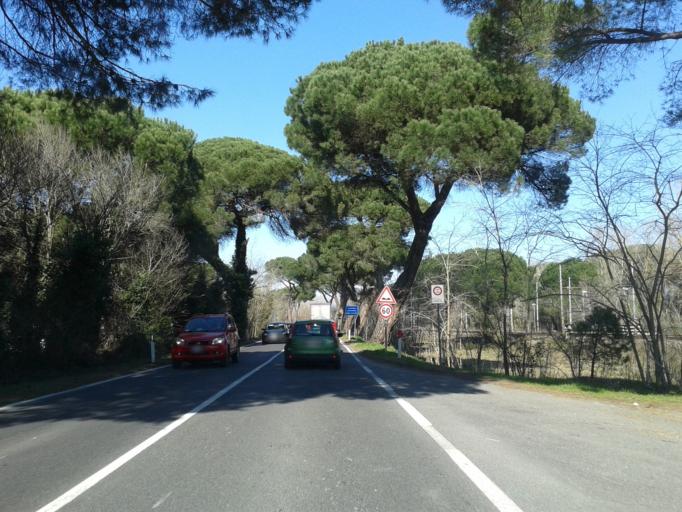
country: IT
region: Tuscany
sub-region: Province of Pisa
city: Marina di Pisa-Tirrenia-Calambrone
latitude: 43.6392
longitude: 10.3564
